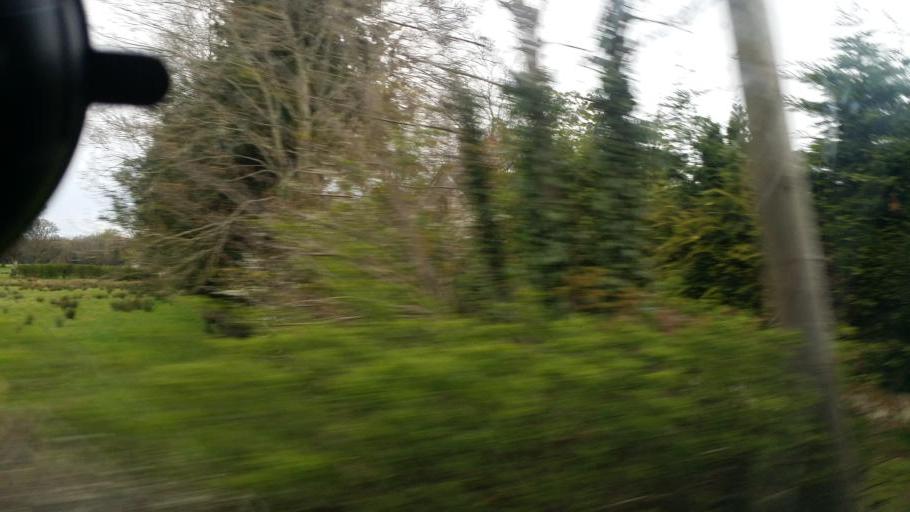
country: IE
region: Ulster
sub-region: An Cabhan
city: Ballyconnell
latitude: 54.0921
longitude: -7.5412
